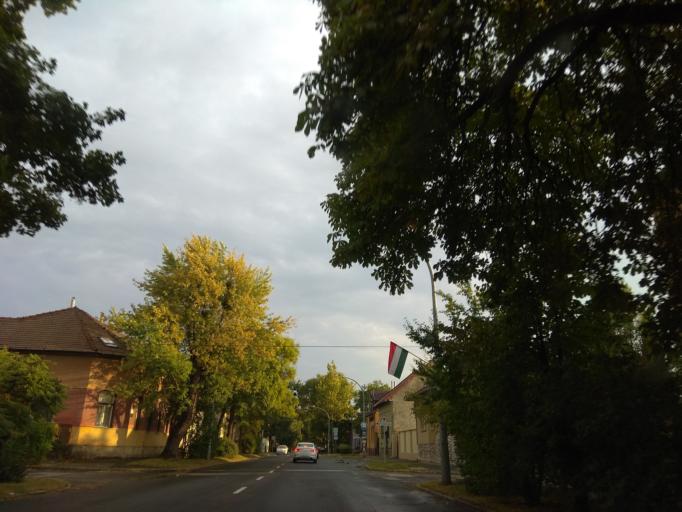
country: HU
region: Borsod-Abauj-Zemplen
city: Miskolc
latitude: 48.0944
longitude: 20.7964
